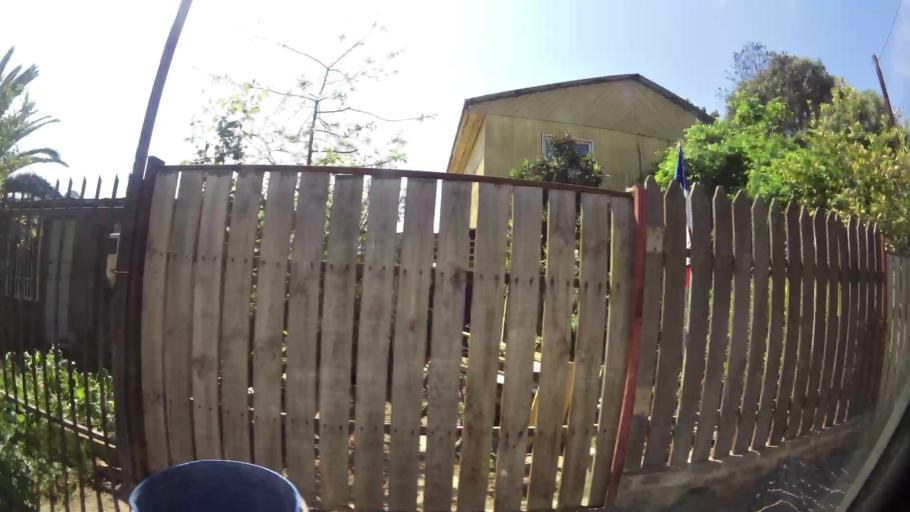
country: CL
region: Santiago Metropolitan
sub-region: Provincia de Talagante
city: Penaflor
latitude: -33.5923
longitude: -70.8146
